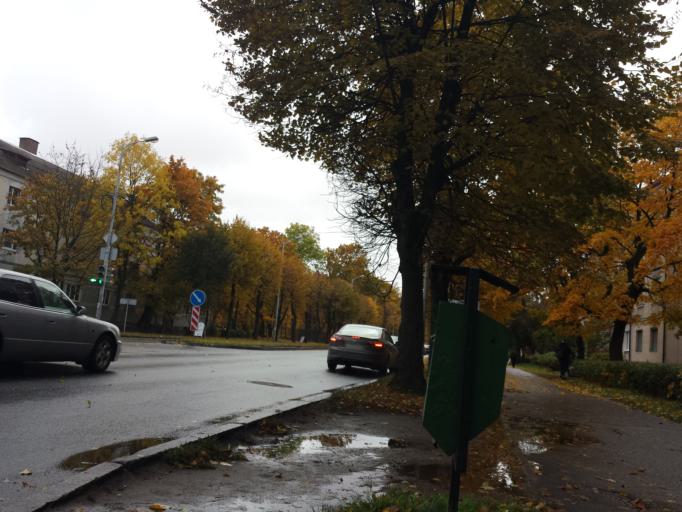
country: RU
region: Kaliningrad
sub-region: Gorod Kaliningrad
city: Kaliningrad
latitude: 54.7264
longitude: 20.5272
